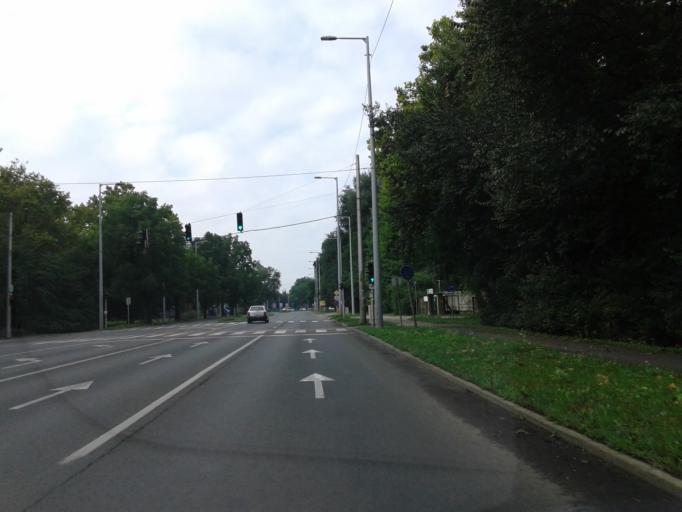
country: HU
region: Csongrad
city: Szeged
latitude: 46.2477
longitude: 20.1655
